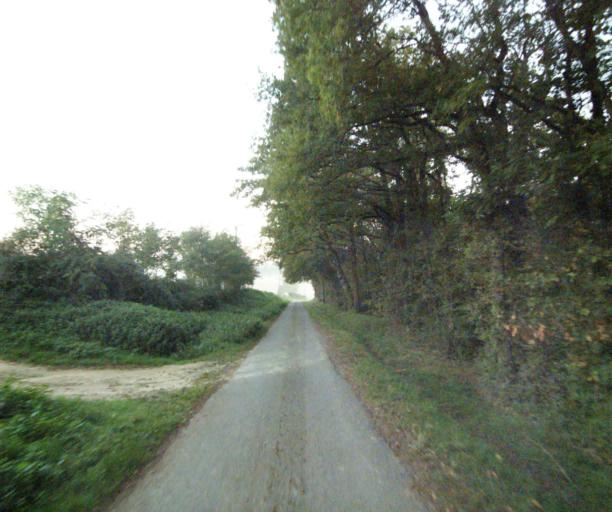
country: FR
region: Midi-Pyrenees
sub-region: Departement du Gers
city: Vic-Fezensac
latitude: 43.7896
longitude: 0.2354
